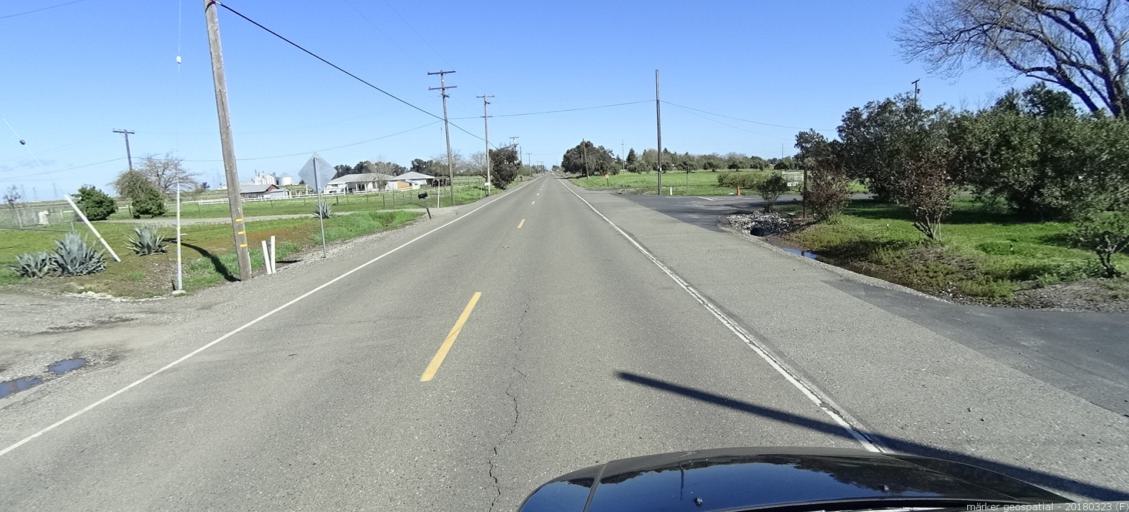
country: US
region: California
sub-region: Sacramento County
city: Elverta
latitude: 38.7347
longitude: -121.4844
